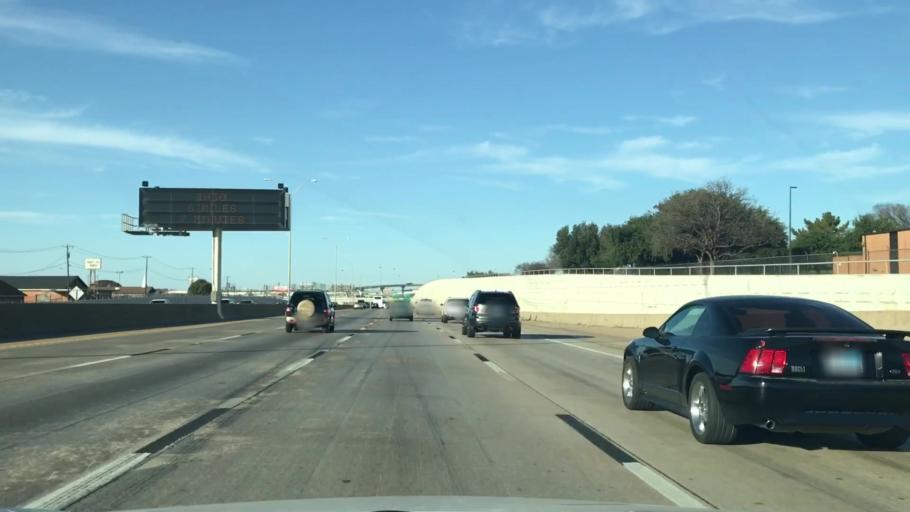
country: US
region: Texas
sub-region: Tarrant County
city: Edgecliff Village
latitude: 32.6551
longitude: -97.3211
